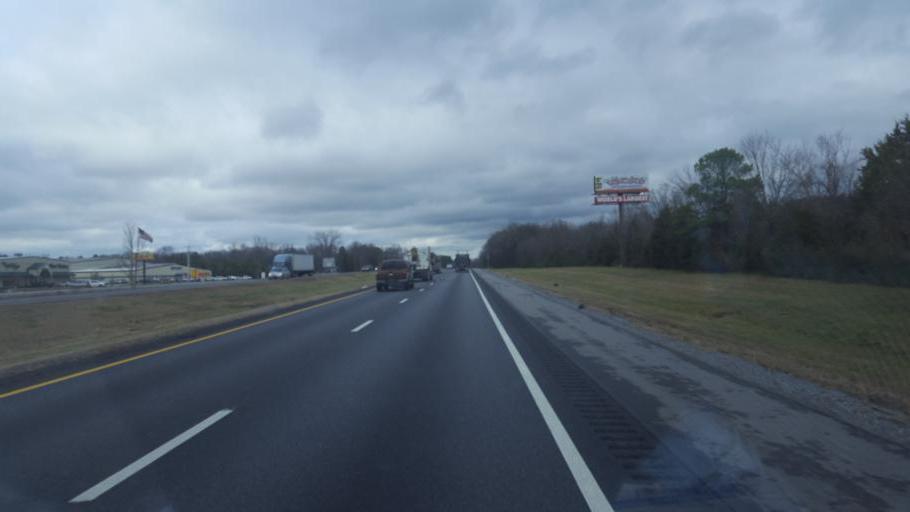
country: US
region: Tennessee
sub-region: Hamilton County
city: Collegedale
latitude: 35.1081
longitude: -85.0502
